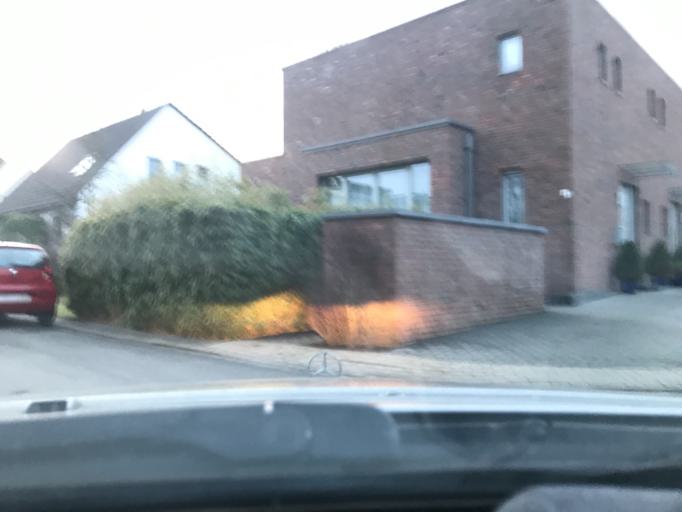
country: DE
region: North Rhine-Westphalia
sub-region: Regierungsbezirk Dusseldorf
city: Krefeld
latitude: 51.3508
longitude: 6.5711
